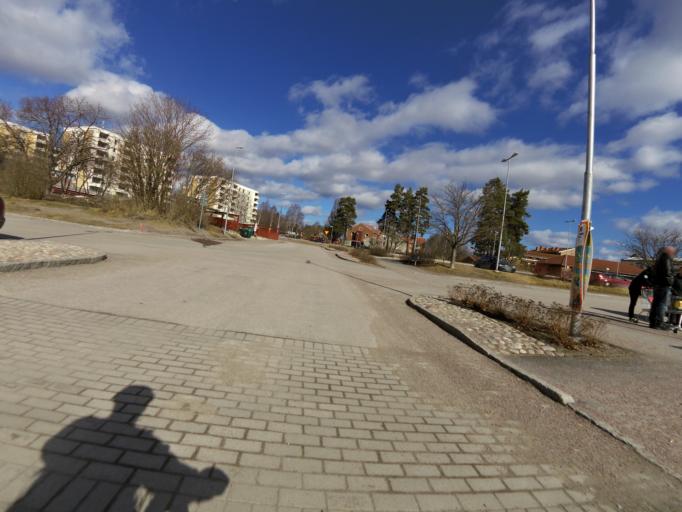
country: SE
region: Gaevleborg
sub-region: Hofors Kommun
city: Hofors
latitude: 60.5466
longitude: 16.2847
